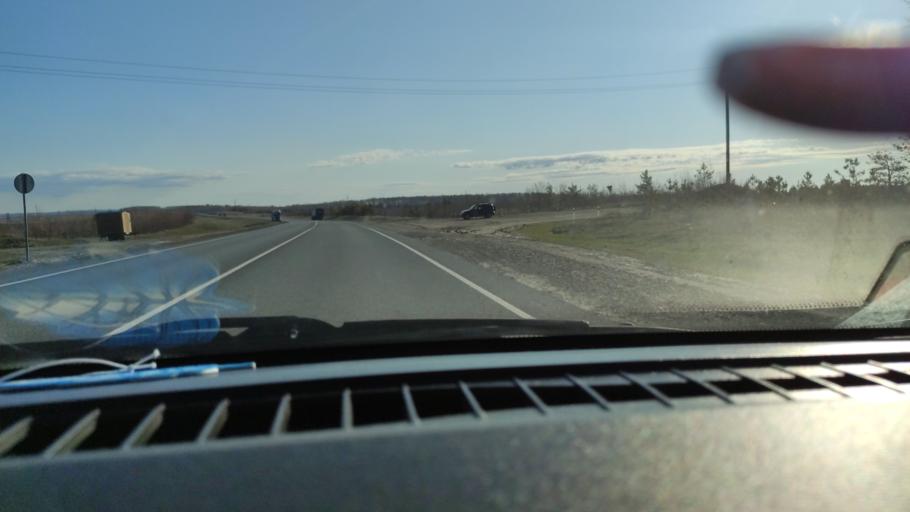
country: RU
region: Saratov
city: Khvalynsk
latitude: 52.5438
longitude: 48.0633
